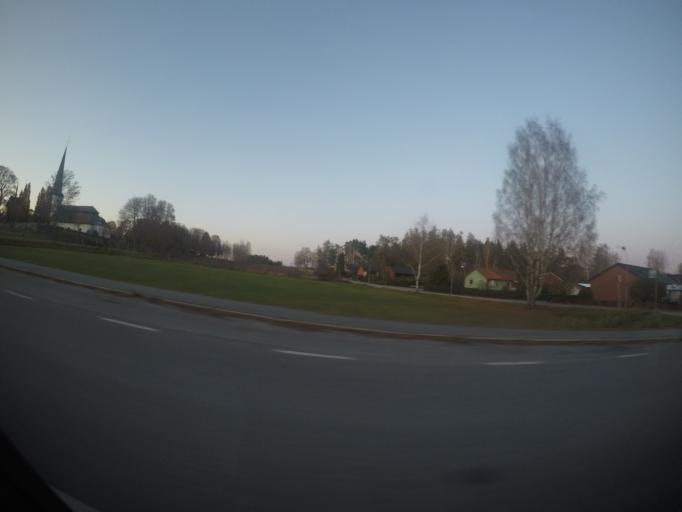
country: SE
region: OErebro
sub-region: Lindesbergs Kommun
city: Frovi
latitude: 59.3182
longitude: 15.4018
